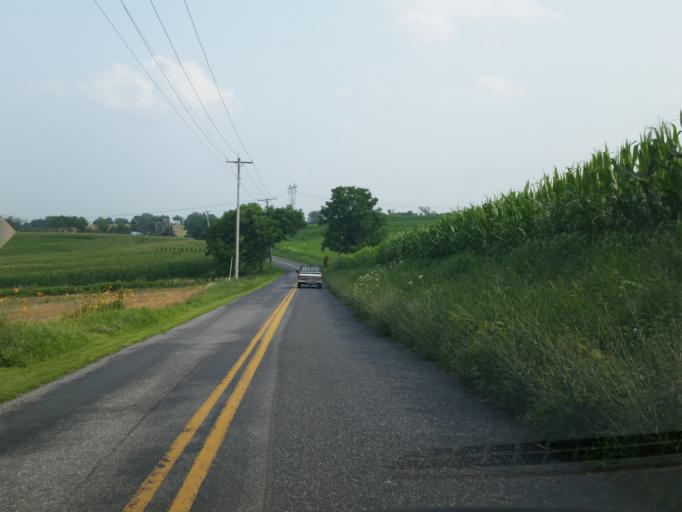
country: US
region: Pennsylvania
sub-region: Lebanon County
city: Palmyra
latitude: 40.3926
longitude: -76.6407
